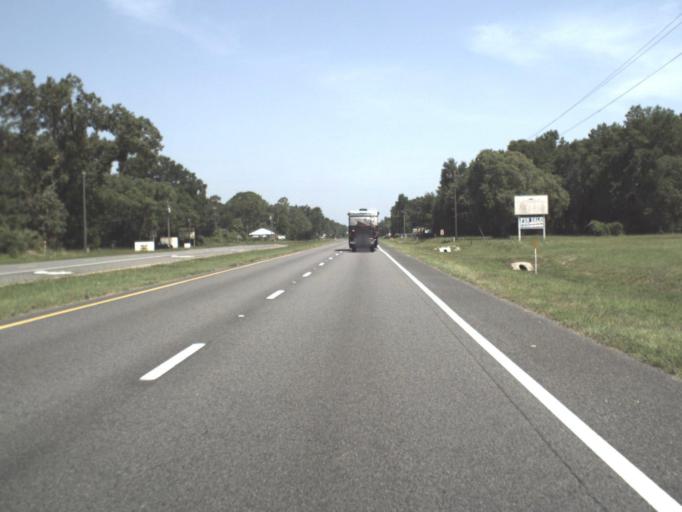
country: US
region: Florida
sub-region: Levy County
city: Manatee Road
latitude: 29.5563
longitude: -82.9035
